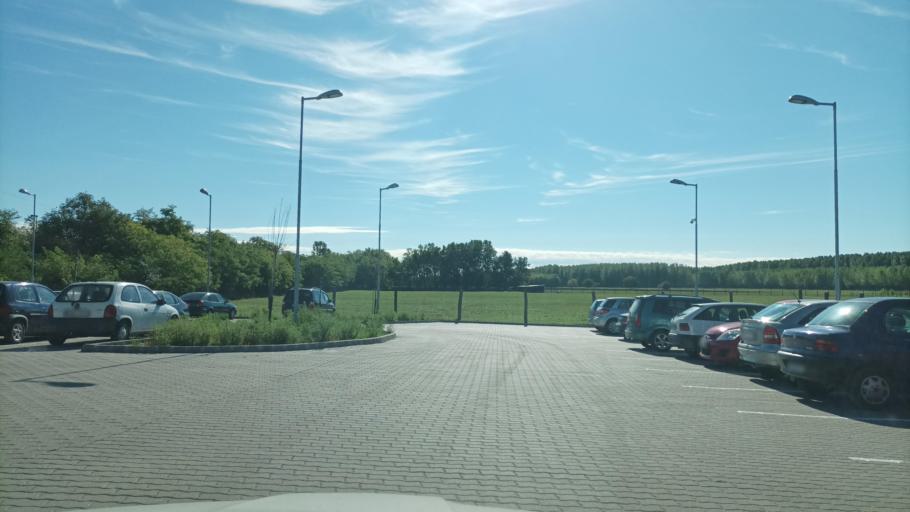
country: HU
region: Pest
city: Cegledbercel
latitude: 47.2161
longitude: 19.6571
